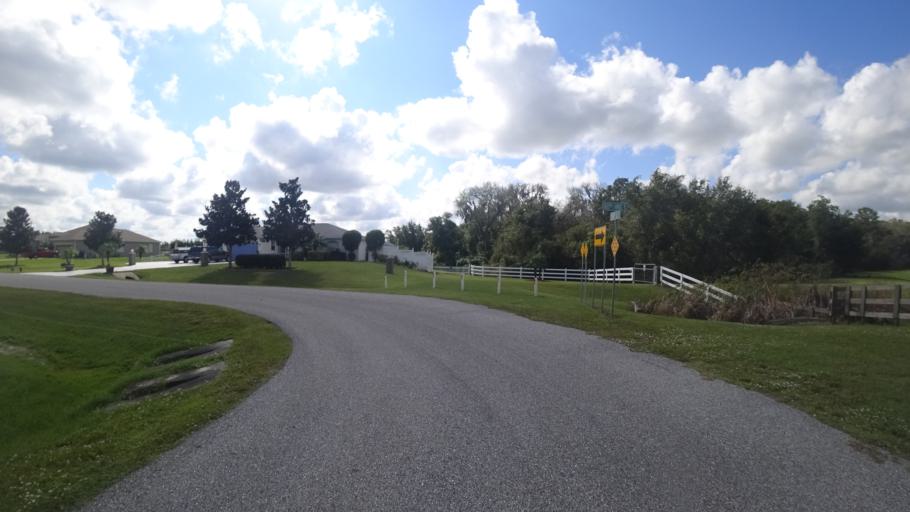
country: US
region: Florida
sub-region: Sarasota County
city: Lake Sarasota
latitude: 27.3923
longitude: -82.2763
